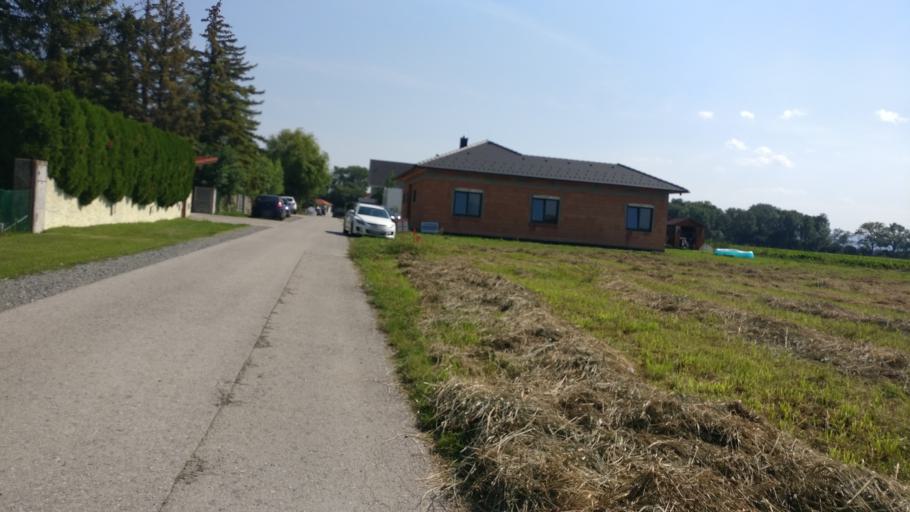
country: AT
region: Lower Austria
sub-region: Politischer Bezirk Baden
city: Mitterndorf an der Fischa
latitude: 47.9777
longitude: 16.4393
